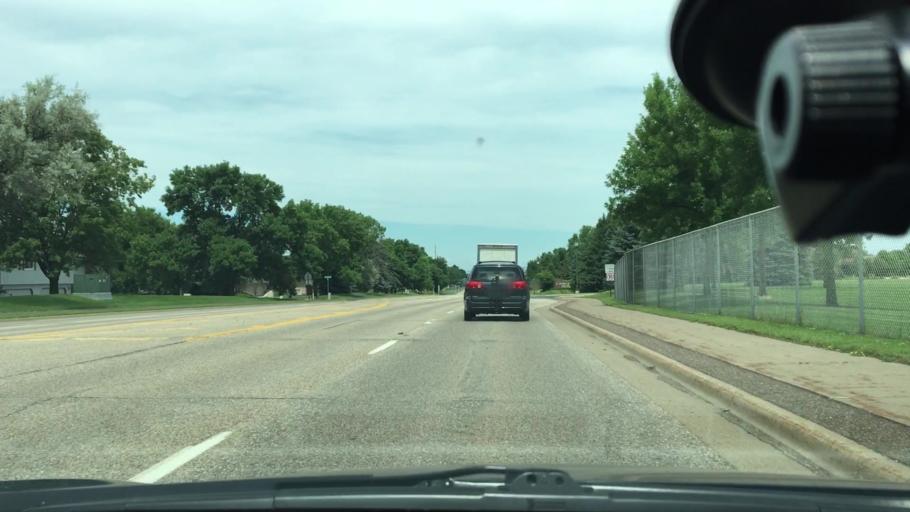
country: US
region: Minnesota
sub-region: Hennepin County
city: Maple Grove
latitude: 45.0828
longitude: -93.4312
